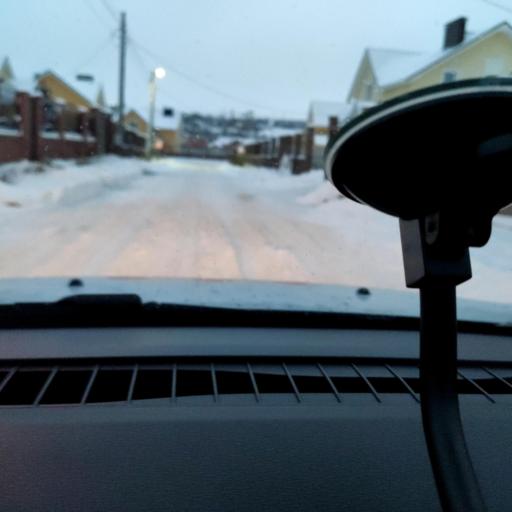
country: RU
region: Samara
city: Kurumoch
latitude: 53.4735
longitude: 50.0092
